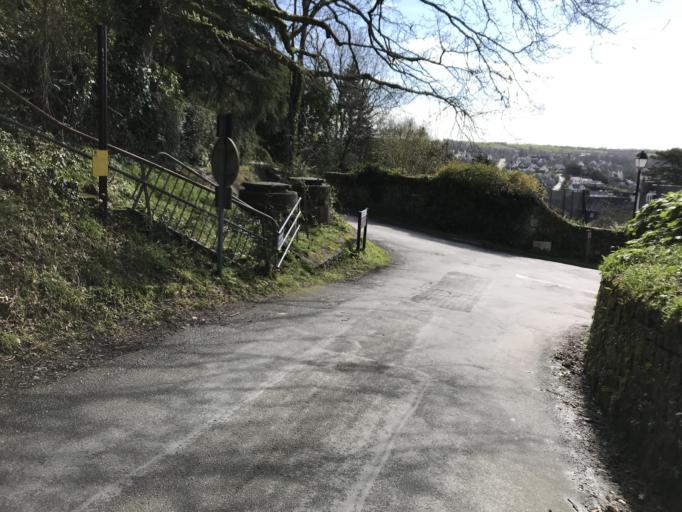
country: FR
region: Brittany
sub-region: Departement du Finistere
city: Daoulas
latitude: 48.3629
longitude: -4.2644
